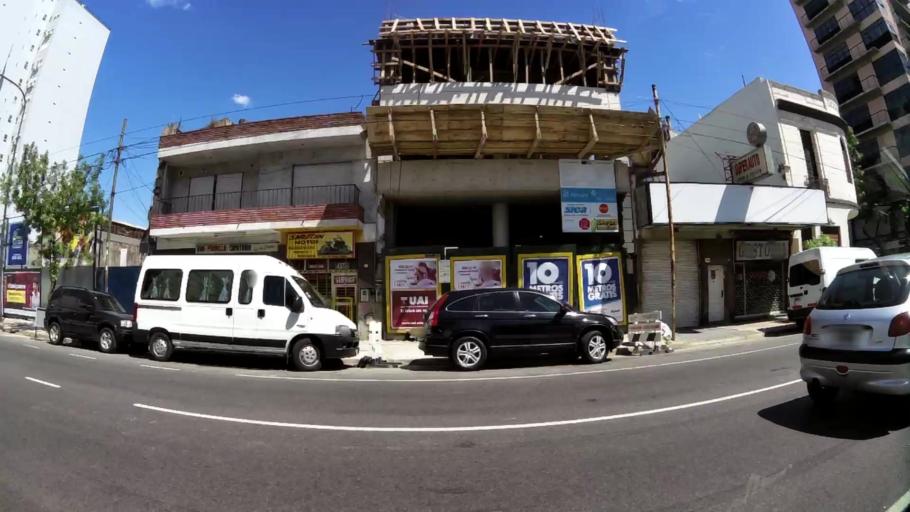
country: AR
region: Buenos Aires F.D.
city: Buenos Aires
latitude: -34.6217
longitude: -58.4250
